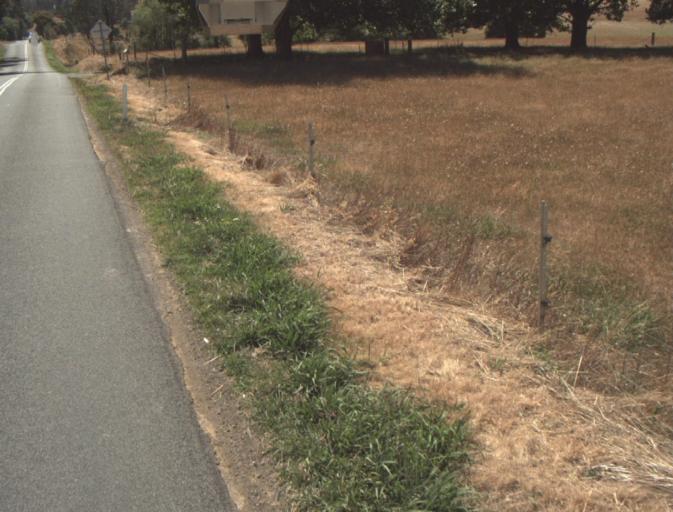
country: AU
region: Tasmania
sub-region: Launceston
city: Mayfield
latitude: -41.2650
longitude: 147.1347
